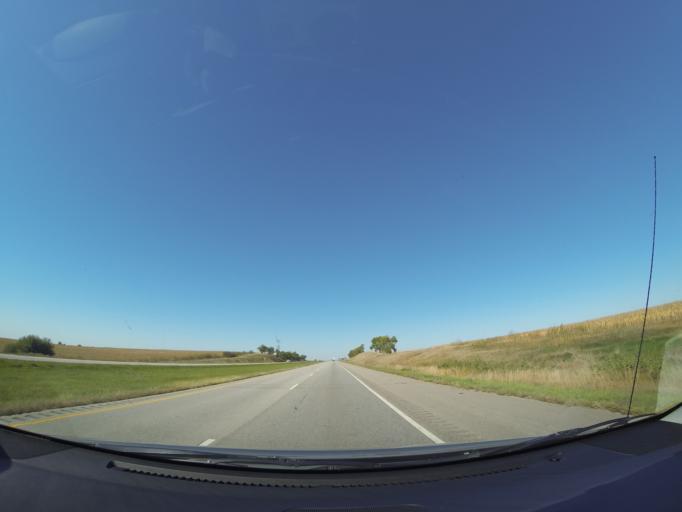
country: US
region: Nebraska
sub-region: Seward County
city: Seward
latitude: 40.8224
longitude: -97.1402
